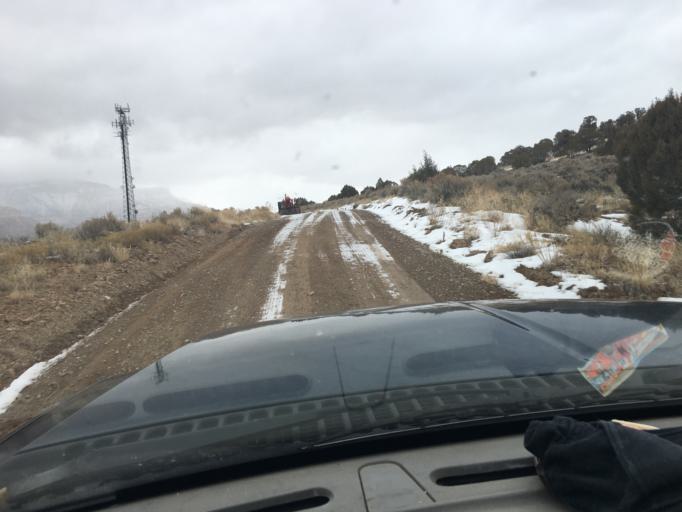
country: US
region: Colorado
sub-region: Garfield County
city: Parachute
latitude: 39.3468
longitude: -108.1717
